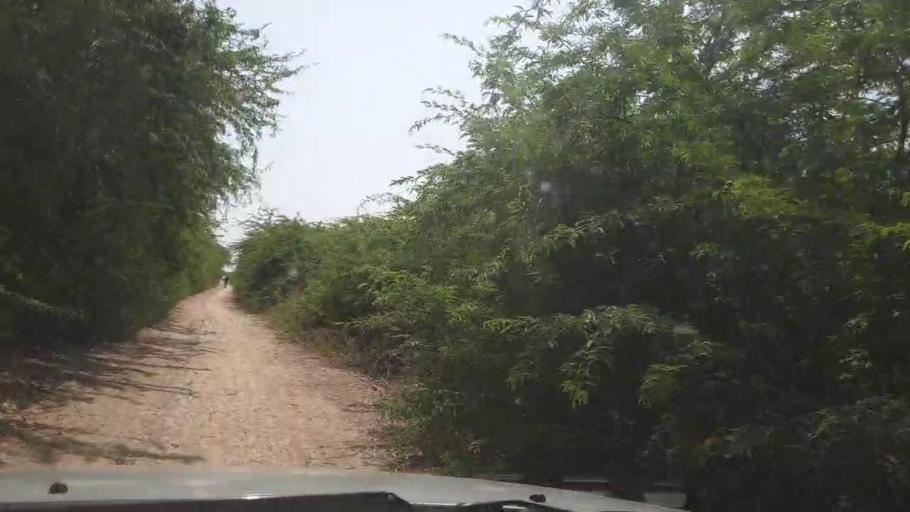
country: PK
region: Sindh
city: Tando Ghulam Ali
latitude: 25.1127
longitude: 68.8101
